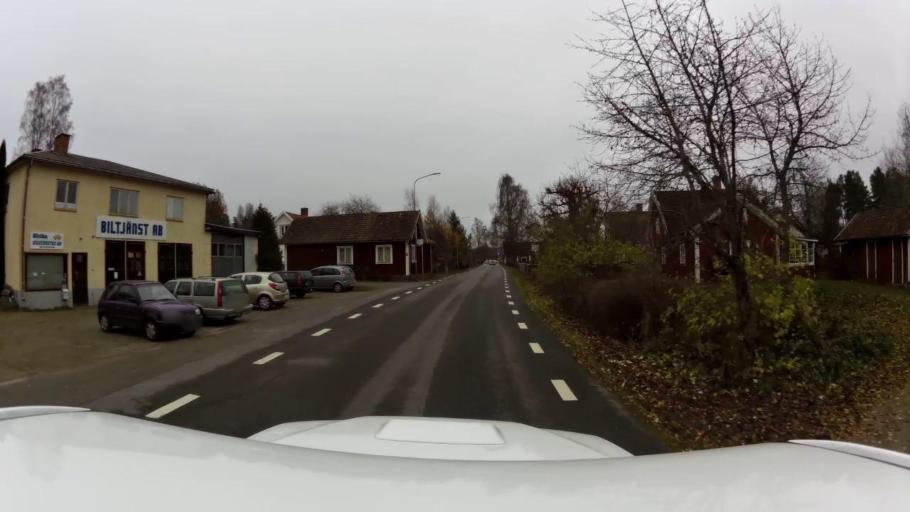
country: SE
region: OEstergoetland
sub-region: Kinda Kommun
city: Kisa
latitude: 58.1279
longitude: 15.4315
